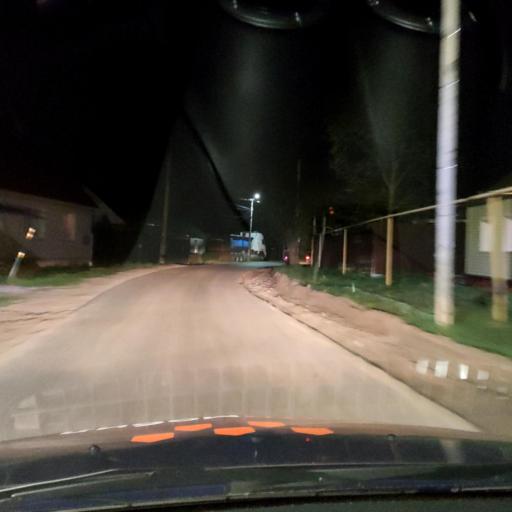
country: RU
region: Voronezj
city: Novaya Usman'
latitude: 51.6394
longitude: 39.3955
